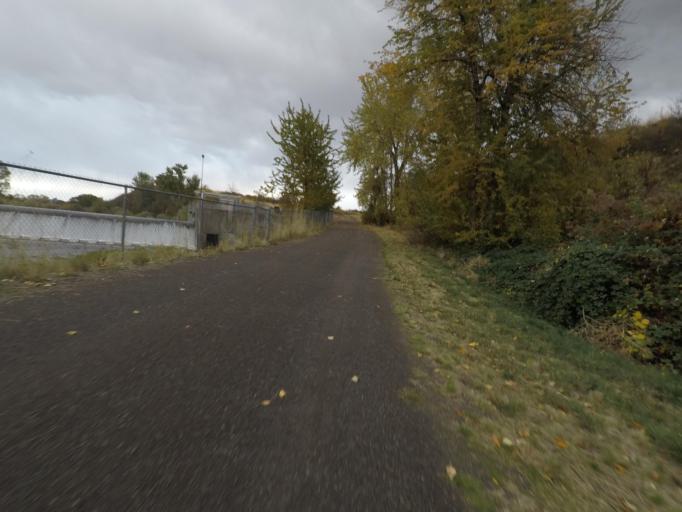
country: US
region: Washington
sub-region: Walla Walla County
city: Walla Walla East
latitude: 46.0796
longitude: -118.2552
